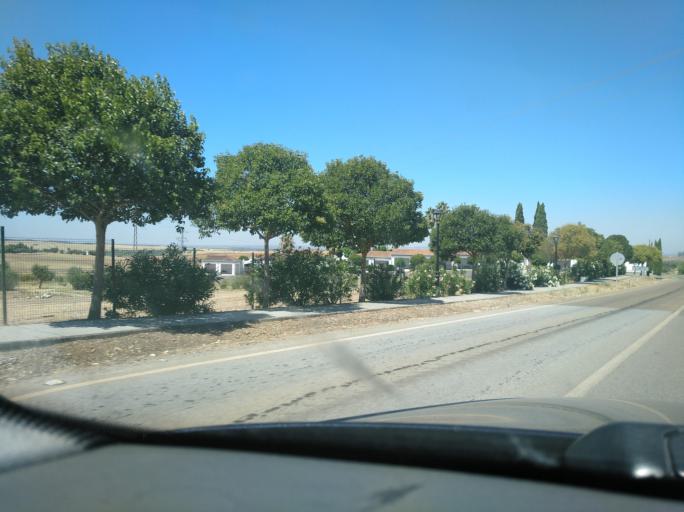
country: ES
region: Extremadura
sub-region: Provincia de Badajoz
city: Olivenza
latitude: 38.6892
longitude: -7.1098
